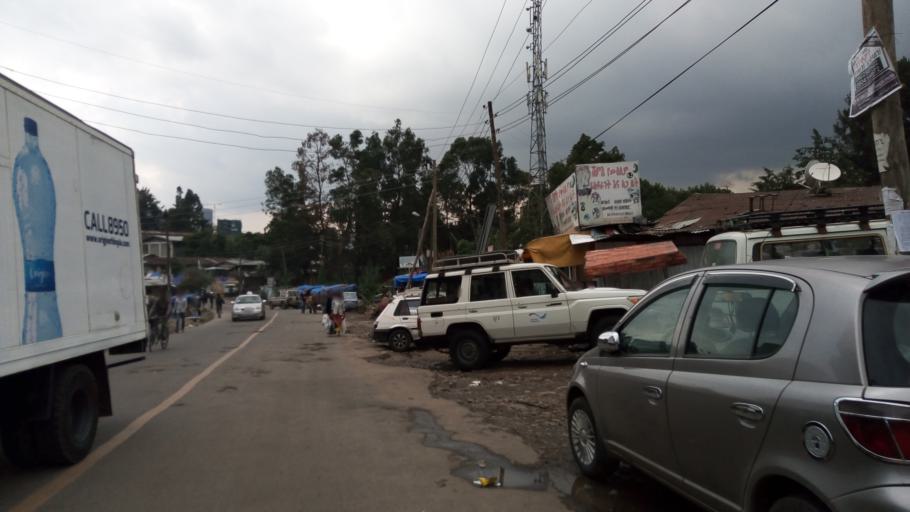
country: ET
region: Adis Abeba
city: Addis Ababa
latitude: 9.0175
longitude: 38.7747
